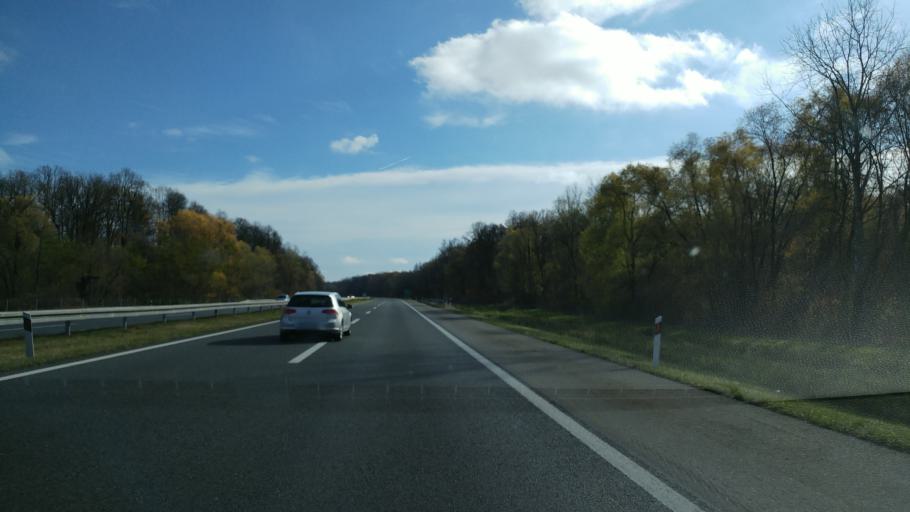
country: HR
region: Sisacko-Moslavacka
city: Lipovljani
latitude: 45.3456
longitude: 16.9170
